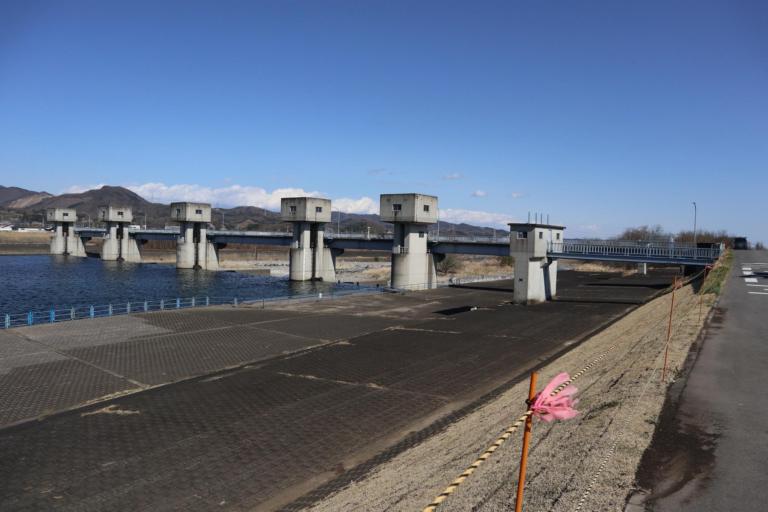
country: JP
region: Gunma
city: Kiryu
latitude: 36.3797
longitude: 139.3510
